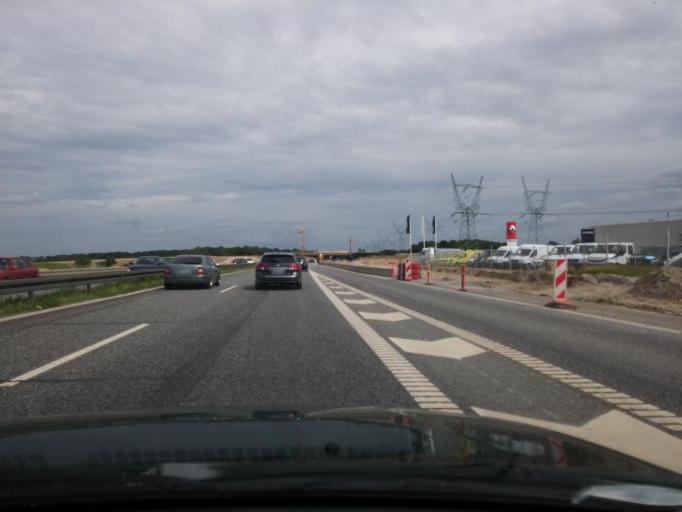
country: DK
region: South Denmark
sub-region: Odense Kommune
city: Hojby
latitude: 55.3510
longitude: 10.4154
